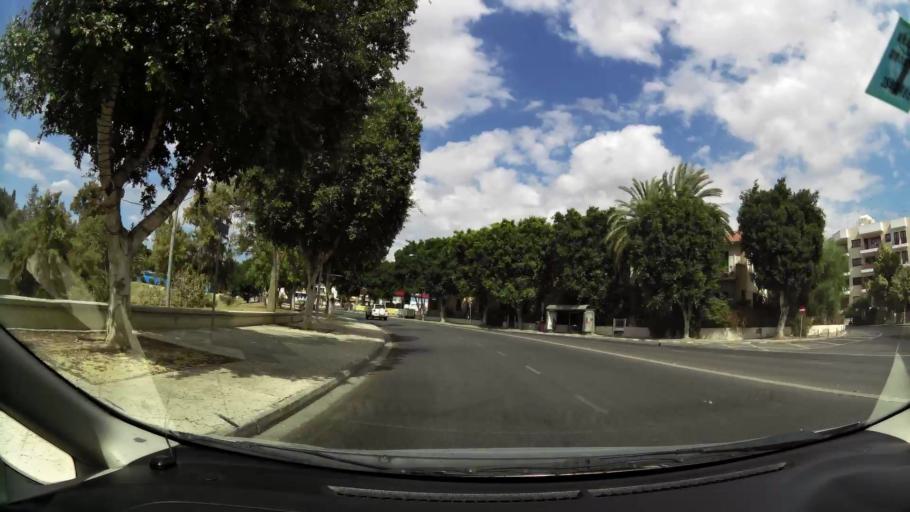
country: CY
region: Lefkosia
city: Nicosia
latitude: 35.1745
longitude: 33.3731
